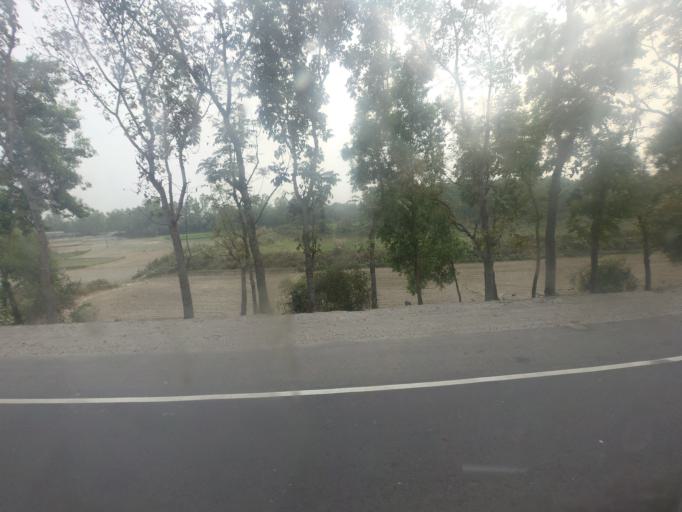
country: BD
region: Dhaka
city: Tangail
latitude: 24.3509
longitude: 89.9069
